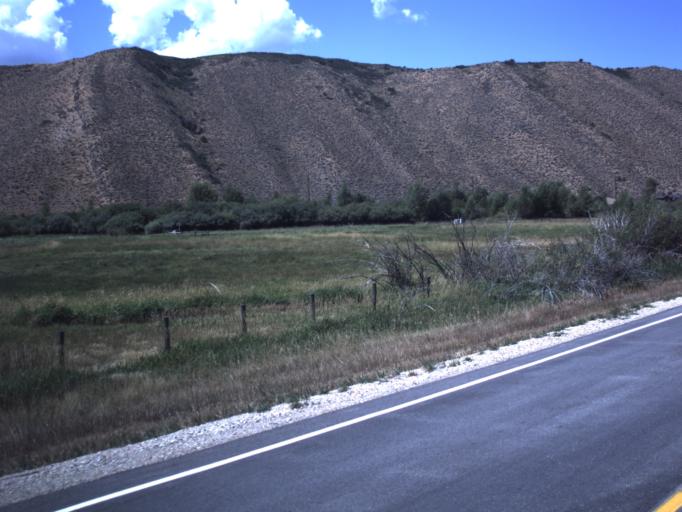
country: US
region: Utah
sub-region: Summit County
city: Oakley
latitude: 40.7493
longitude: -111.3660
